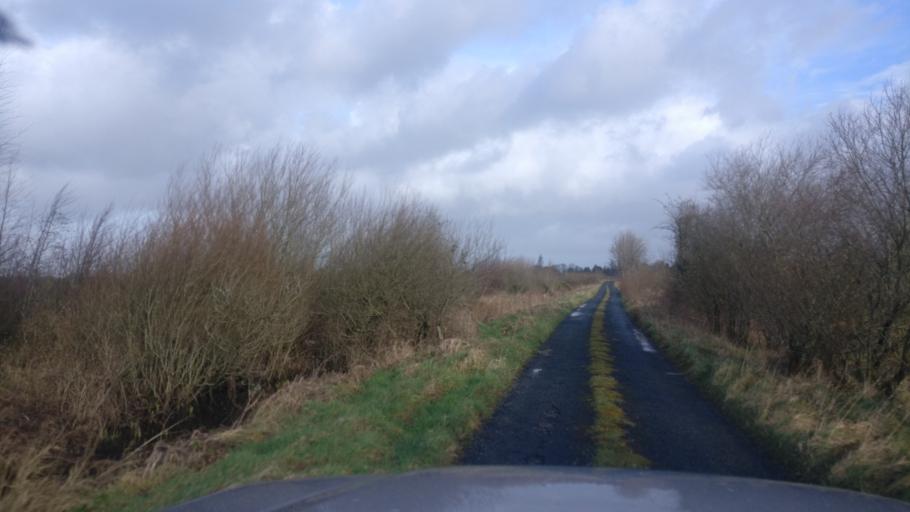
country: IE
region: Connaught
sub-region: County Galway
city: Loughrea
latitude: 53.2338
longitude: -8.5350
